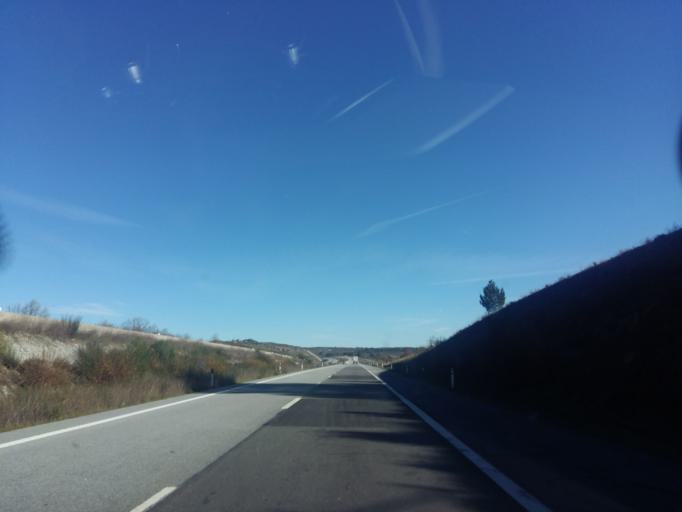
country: PT
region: Guarda
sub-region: Guarda
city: Sequeira
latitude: 40.5810
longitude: -7.1666
